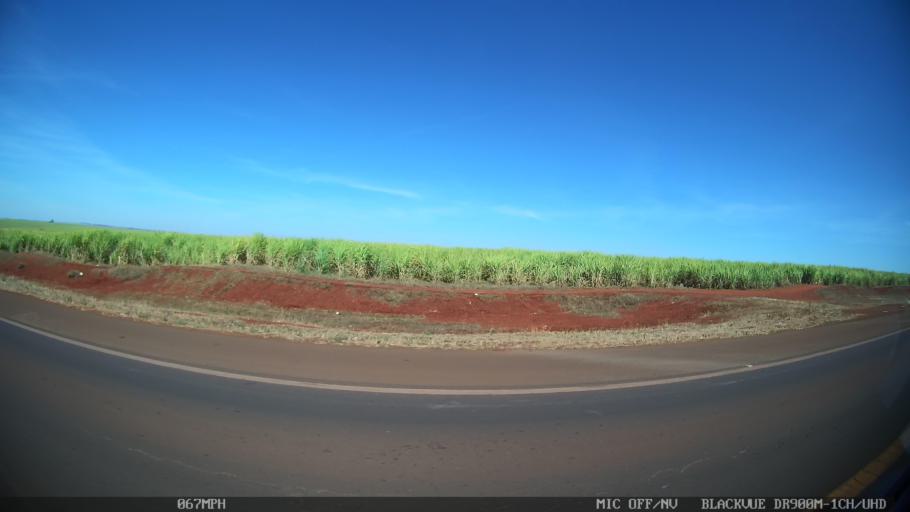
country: BR
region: Sao Paulo
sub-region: Ipua
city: Ipua
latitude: -20.4939
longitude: -48.0389
